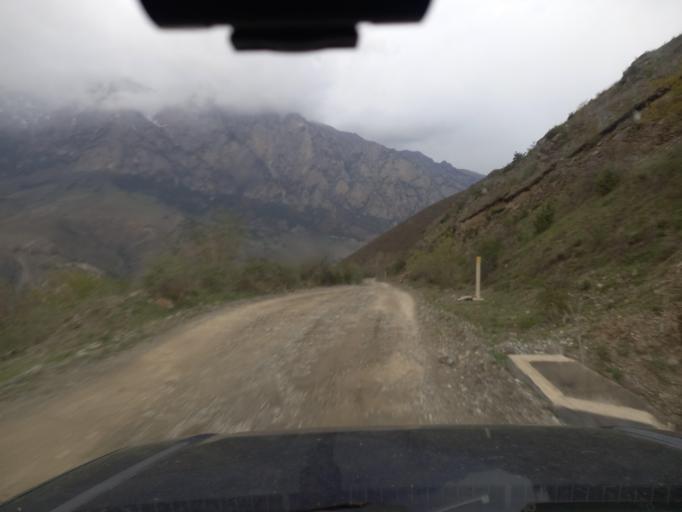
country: RU
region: North Ossetia
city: Mizur
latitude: 42.8506
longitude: 44.1623
